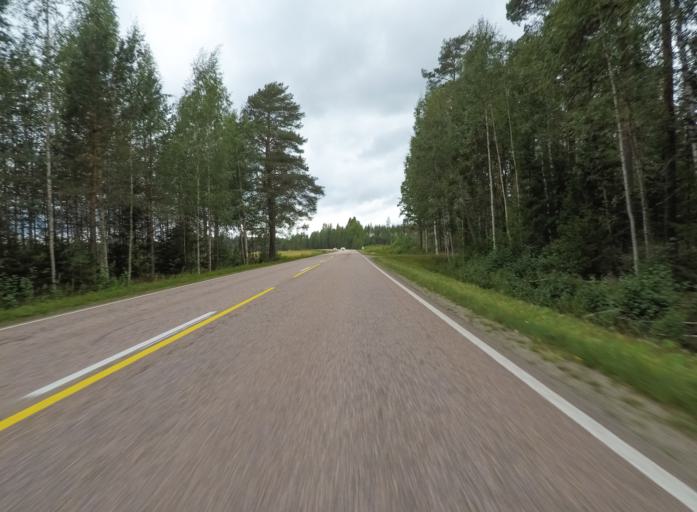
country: FI
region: Central Finland
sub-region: Jyvaeskylae
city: Hankasalmi
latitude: 62.3606
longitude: 26.5465
